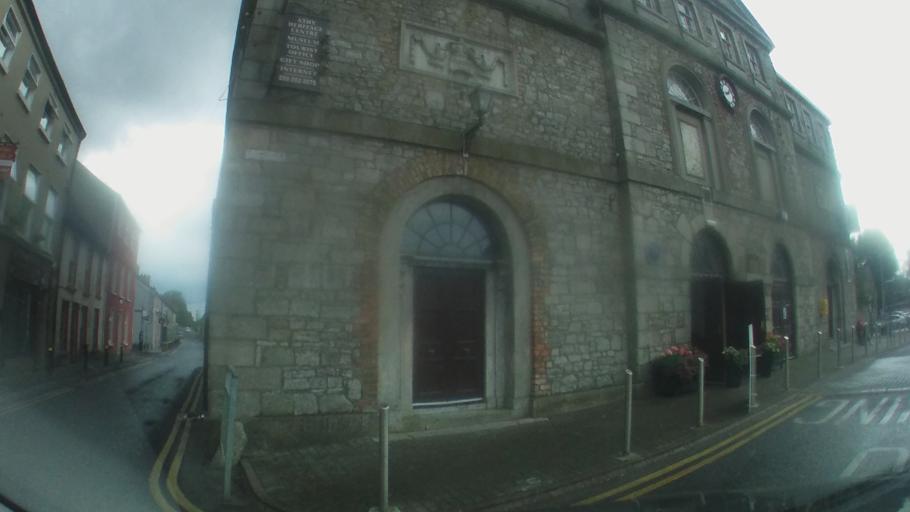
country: IE
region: Leinster
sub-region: Kildare
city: Athy
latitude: 52.9919
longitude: -6.9831
